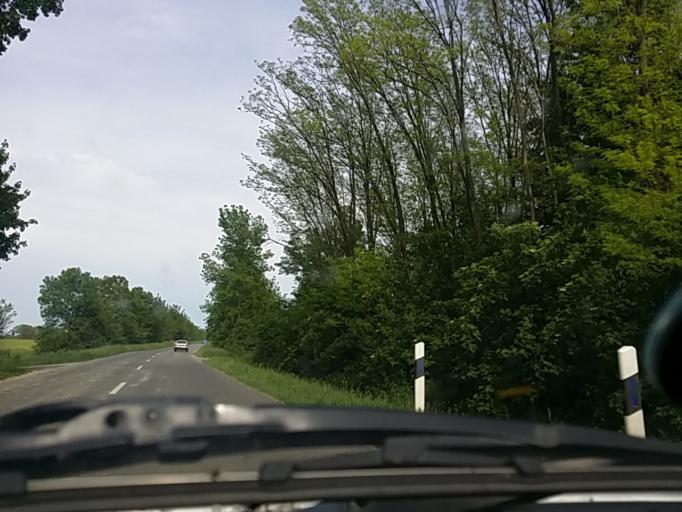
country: HR
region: Osjecko-Baranjska
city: Viljevo
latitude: 45.8278
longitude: 18.1085
